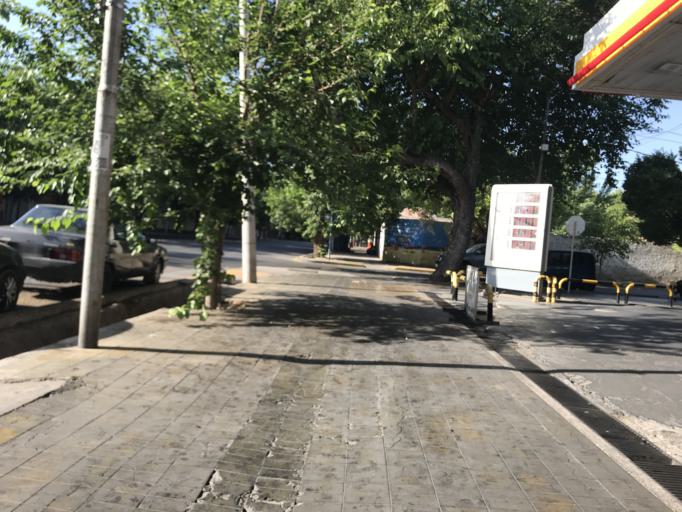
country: AR
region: Mendoza
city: Mendoza
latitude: -32.8815
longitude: -68.8425
